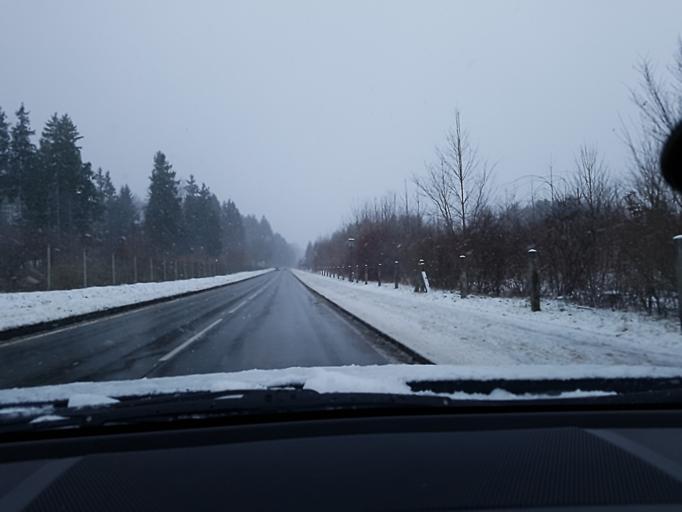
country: AT
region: Salzburg
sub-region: Politischer Bezirk Salzburg-Umgebung
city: Grodig
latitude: 47.7452
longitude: 13.0254
